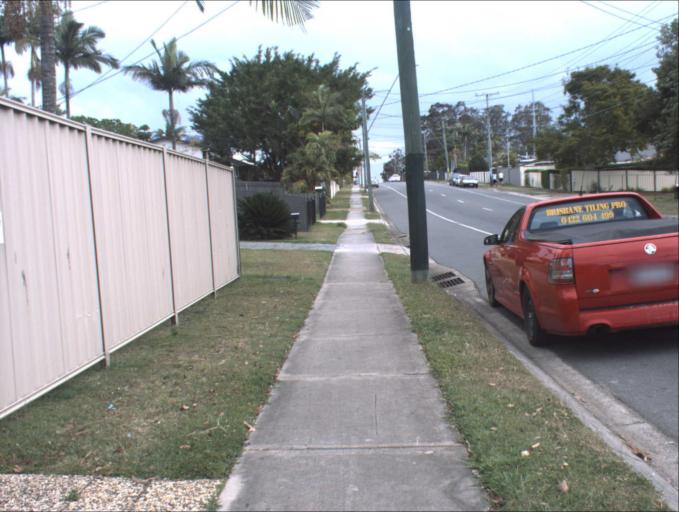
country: AU
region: Queensland
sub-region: Logan
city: Slacks Creek
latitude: -27.6408
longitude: 153.1541
